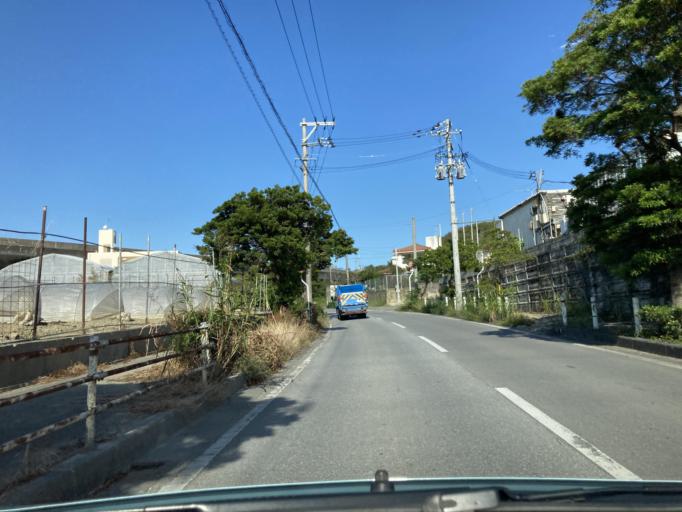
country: JP
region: Okinawa
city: Tomigusuku
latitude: 26.1736
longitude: 127.7048
